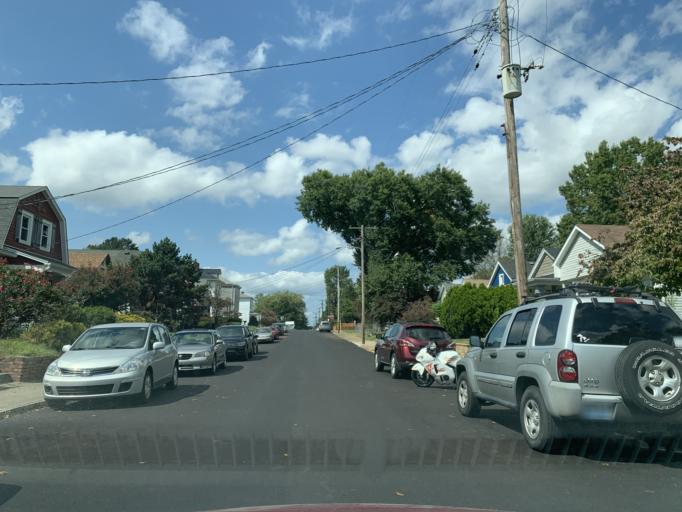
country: US
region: Kentucky
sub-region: Jefferson County
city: Audubon Park
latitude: 38.2295
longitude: -85.7346
